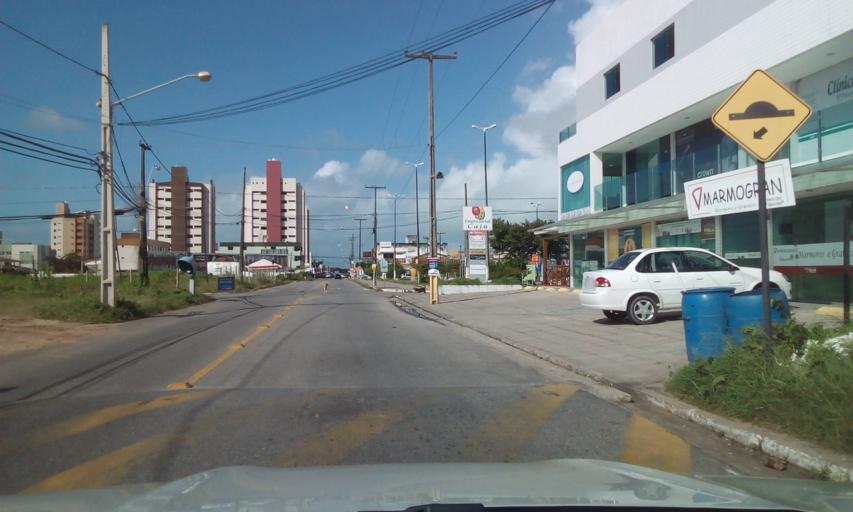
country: BR
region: Paraiba
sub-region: Joao Pessoa
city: Joao Pessoa
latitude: -7.0683
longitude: -34.8449
